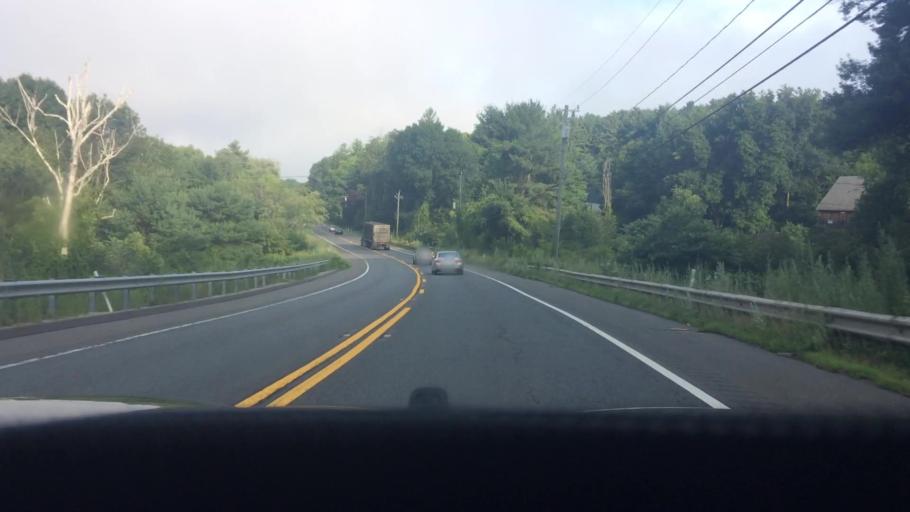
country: US
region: Massachusetts
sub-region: Franklin County
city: Turners Falls
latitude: 42.6082
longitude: -72.5332
